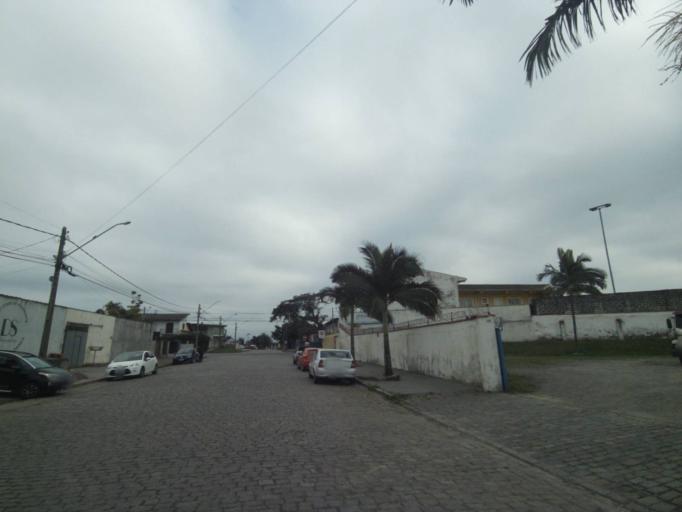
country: BR
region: Parana
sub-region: Paranagua
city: Paranagua
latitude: -25.5132
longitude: -48.5191
